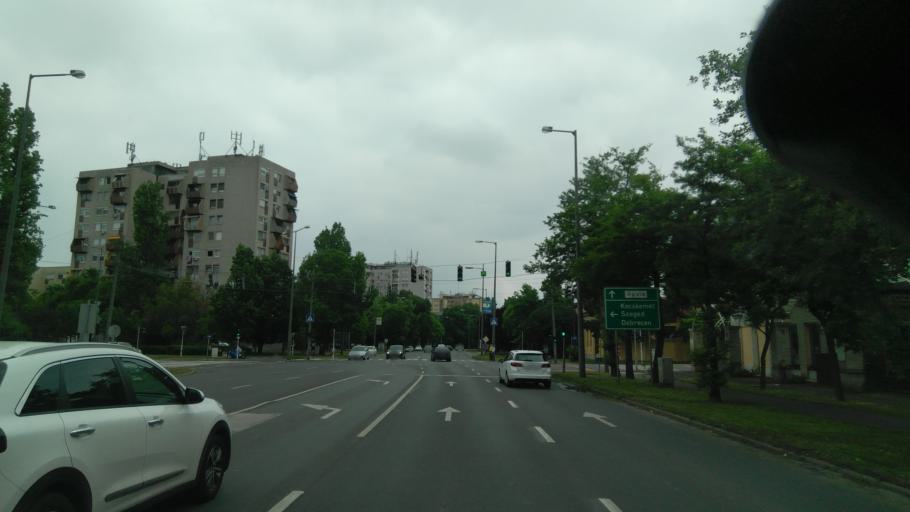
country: HU
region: Bekes
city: Bekescsaba
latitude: 46.6733
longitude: 21.0913
